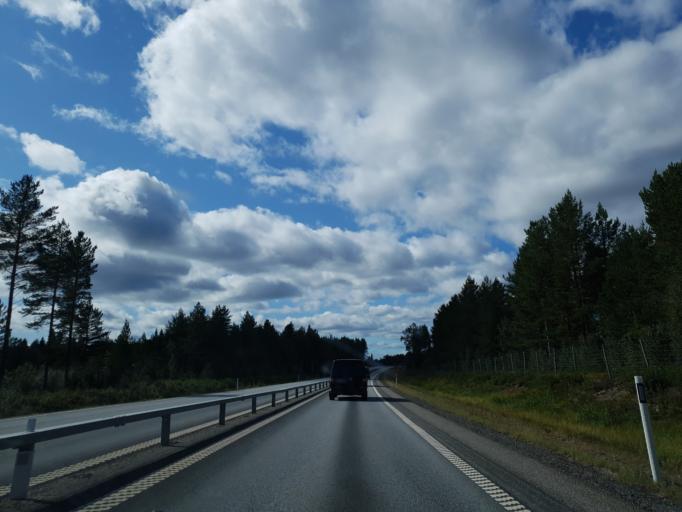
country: SE
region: Vaesterbotten
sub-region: Umea Kommun
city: Hoernefors
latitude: 63.6011
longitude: 19.7553
